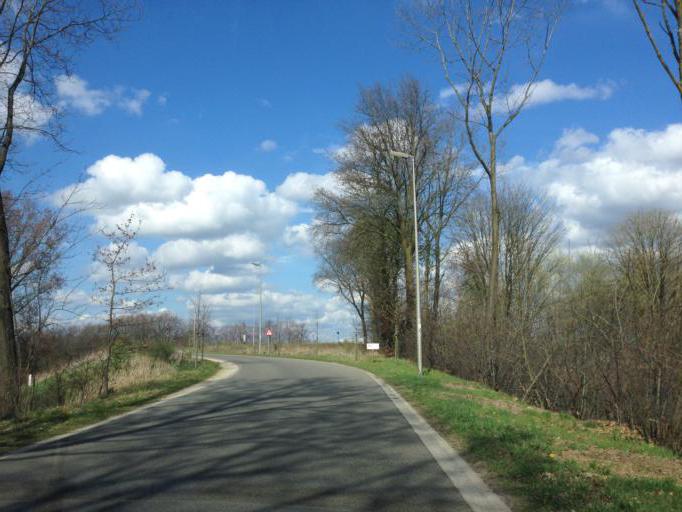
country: BE
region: Flanders
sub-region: Provincie Limburg
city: Bree
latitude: 51.1617
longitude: 5.6079
